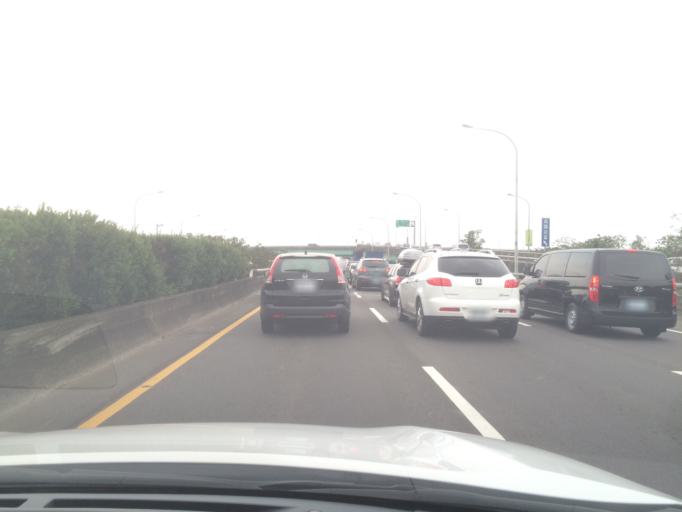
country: TW
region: Taiwan
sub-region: Taichung City
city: Taichung
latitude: 24.1226
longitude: 120.6197
